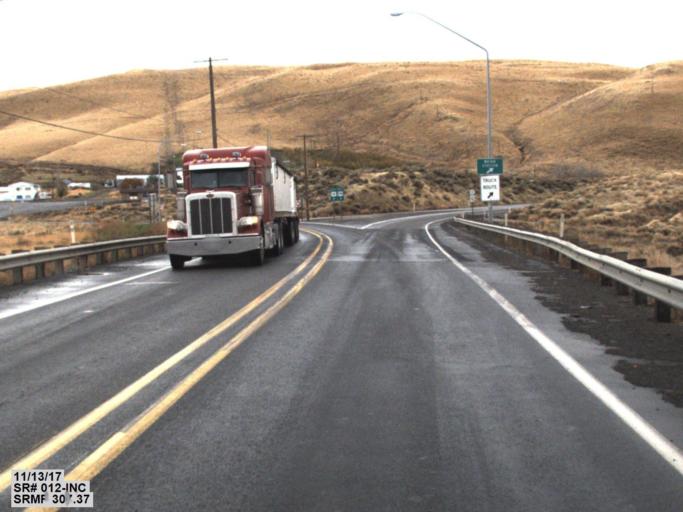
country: US
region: Washington
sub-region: Benton County
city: Finley
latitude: 46.0598
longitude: -118.9098
